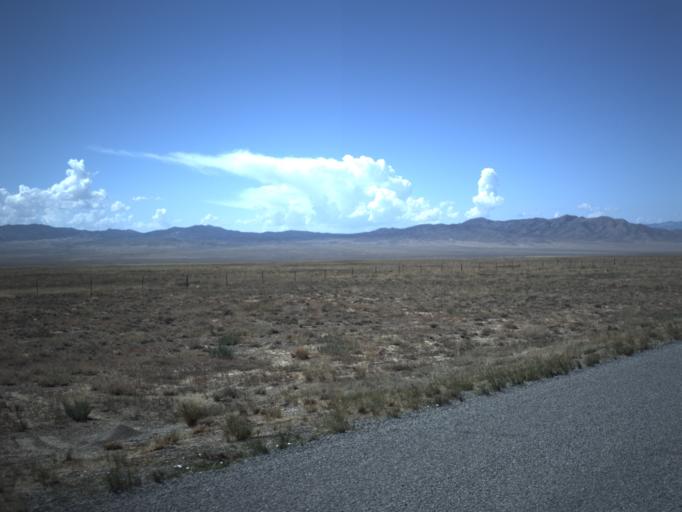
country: US
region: Utah
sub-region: Beaver County
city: Milford
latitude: 39.0593
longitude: -113.7592
